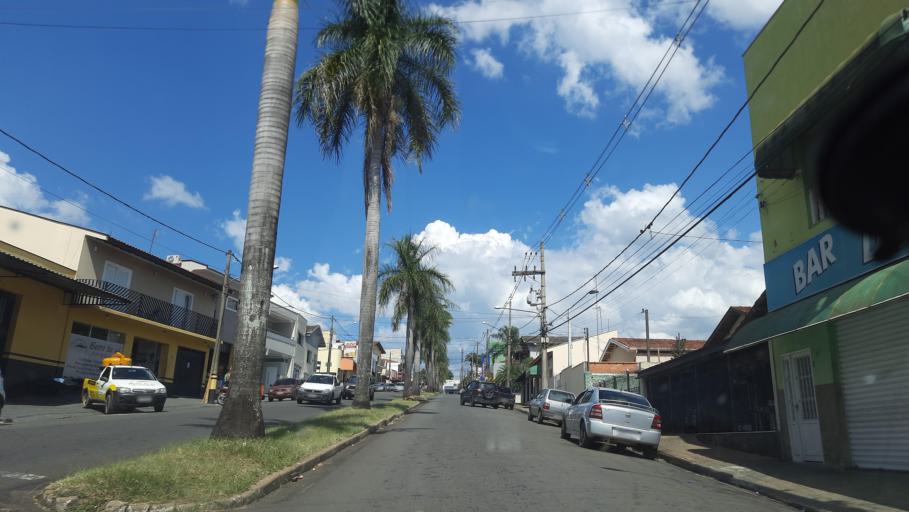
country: BR
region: Sao Paulo
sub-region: Sao Jose Do Rio Pardo
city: Sao Jose do Rio Pardo
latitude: -21.6028
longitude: -46.9010
